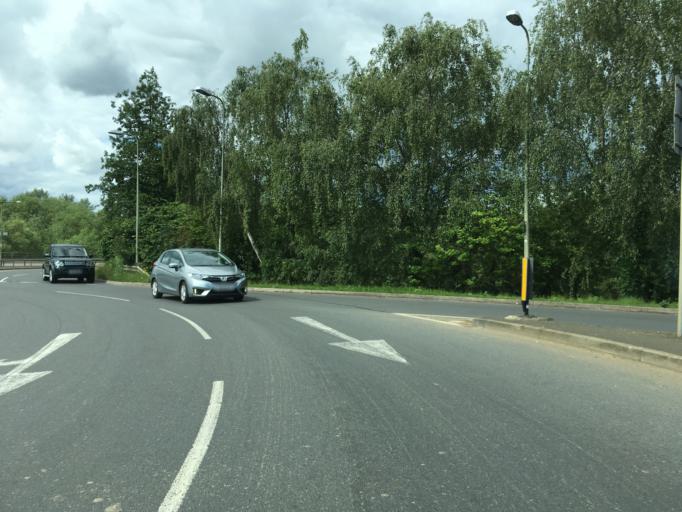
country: GB
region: England
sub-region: Oxfordshire
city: Banbury
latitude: 52.0714
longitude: -1.3307
